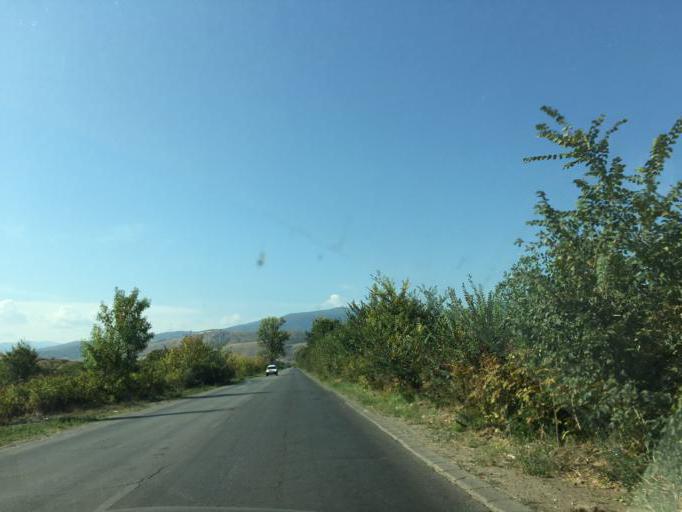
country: BG
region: Pazardzhik
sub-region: Obshtina Pazardzhik
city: Pazardzhik
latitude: 42.1435
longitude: 24.3023
